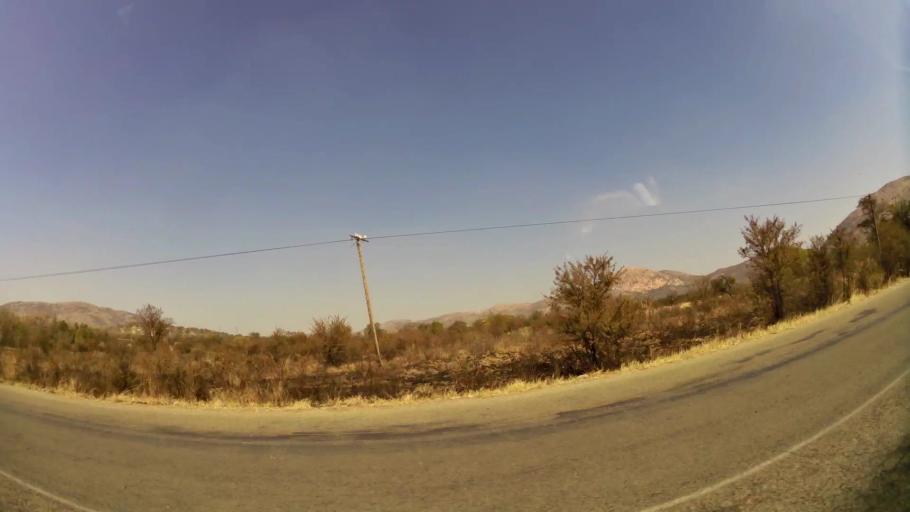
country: ZA
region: North-West
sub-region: Bojanala Platinum District Municipality
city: Rustenburg
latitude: -25.6343
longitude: 27.1630
